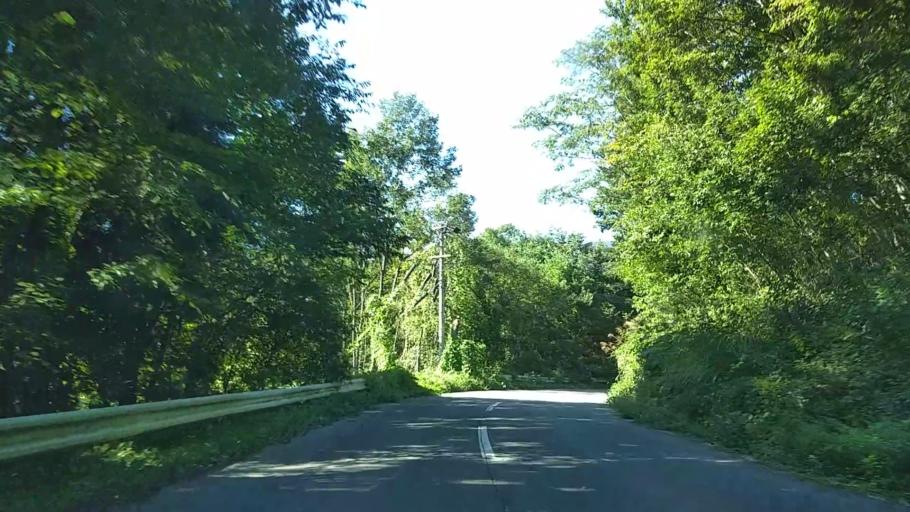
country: JP
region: Nagano
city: Nagano-shi
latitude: 36.6035
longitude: 138.0933
